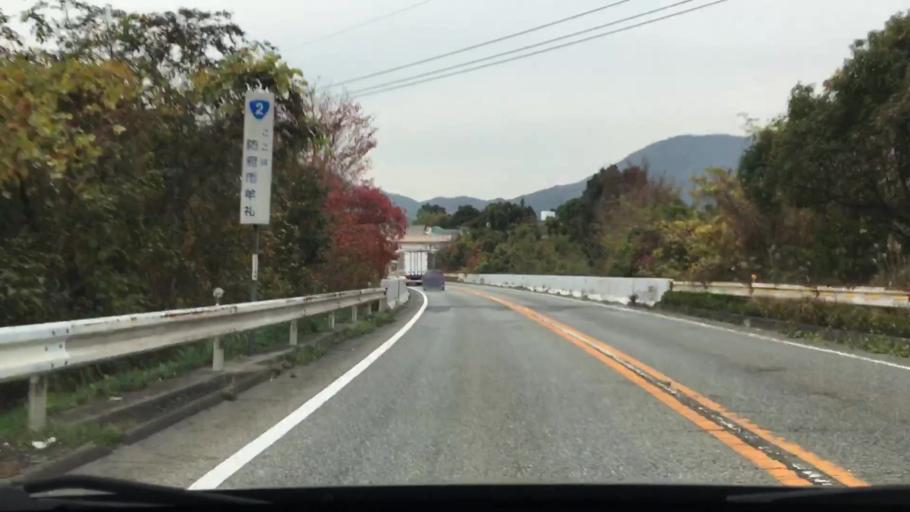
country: JP
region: Yamaguchi
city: Hofu
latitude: 34.0563
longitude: 131.6157
